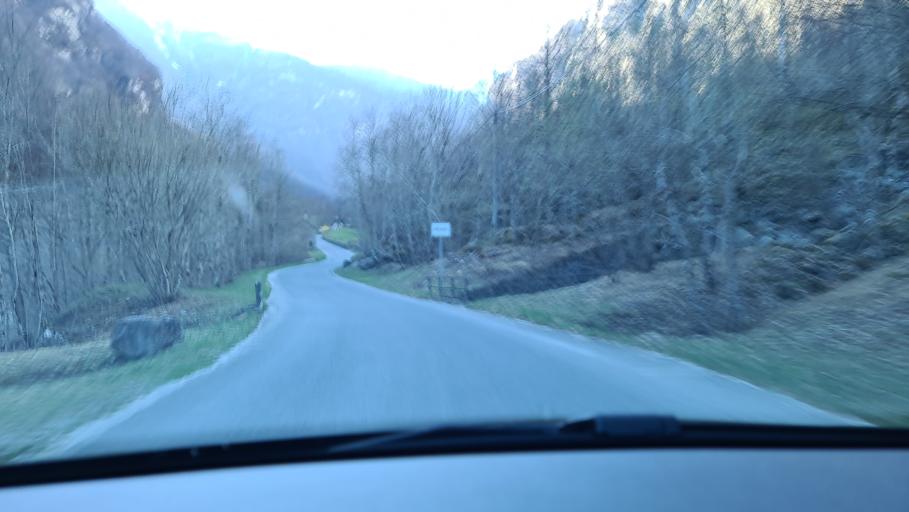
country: CH
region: Ticino
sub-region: Vallemaggia District
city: Cevio
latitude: 46.3635
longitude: 8.5710
